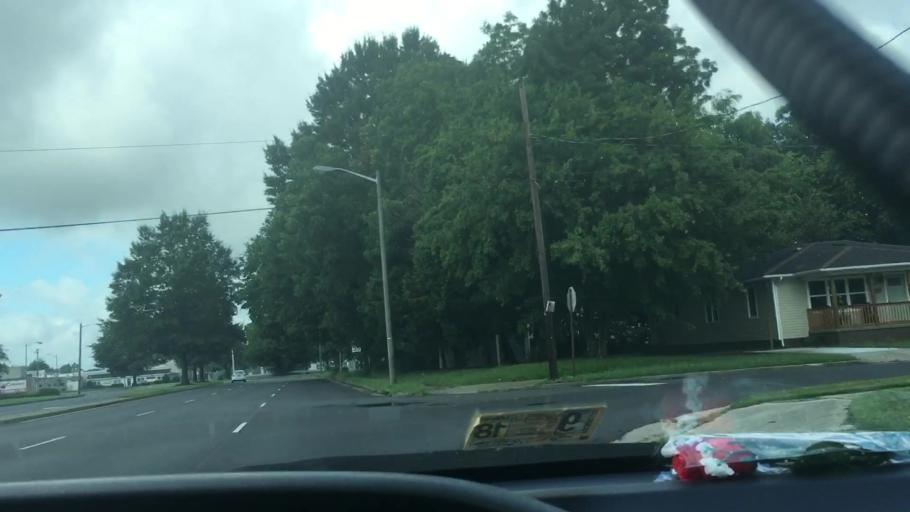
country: US
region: Virginia
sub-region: City of Portsmouth
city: Portsmouth Heights
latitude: 36.8367
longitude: -76.3367
